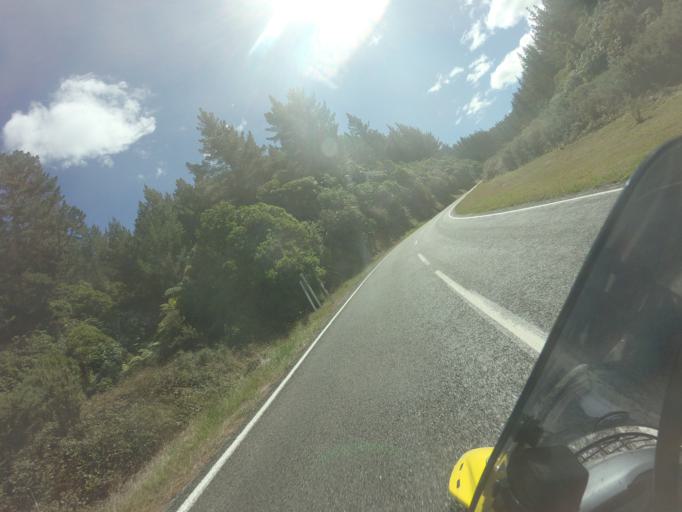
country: NZ
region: Bay of Plenty
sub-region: Kawerau District
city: Kawerau
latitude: -38.1765
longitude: 176.8285
